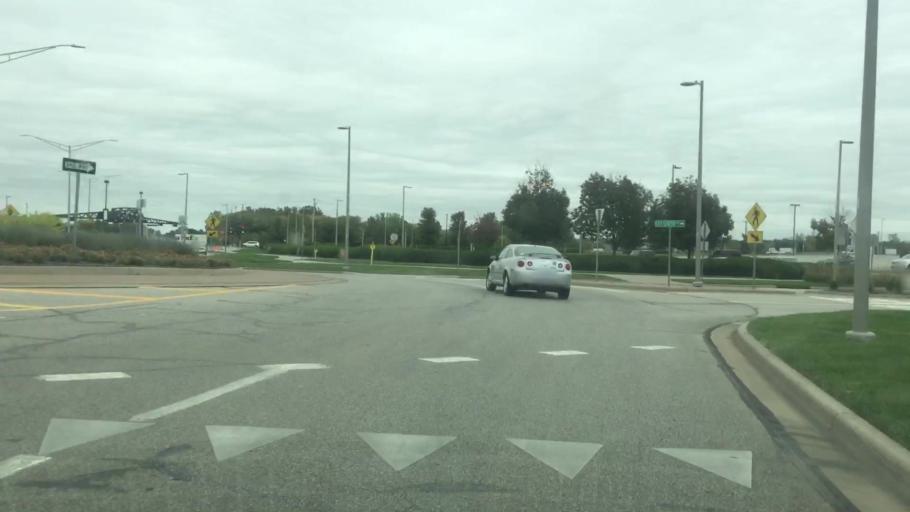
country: US
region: Kansas
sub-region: Johnson County
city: Lenexa
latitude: 38.9689
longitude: -94.7796
